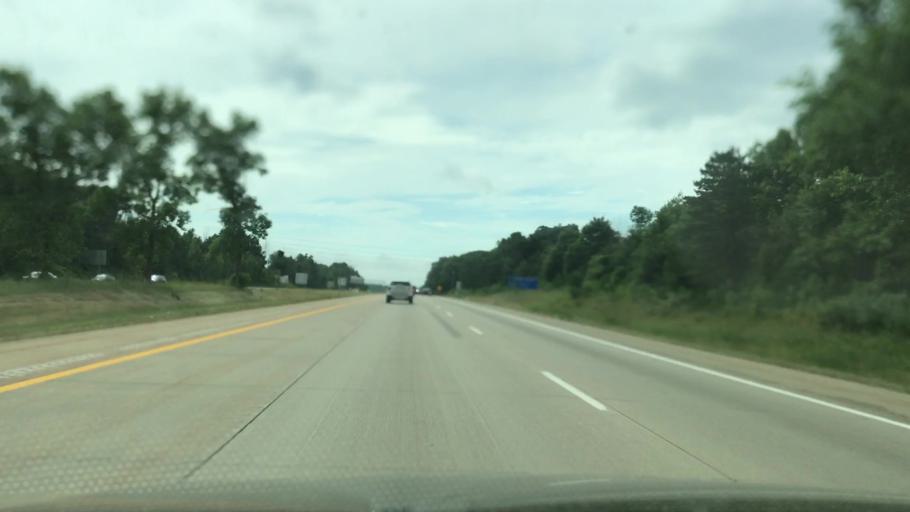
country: US
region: Michigan
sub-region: Kent County
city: Comstock Park
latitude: 43.0194
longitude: -85.7021
